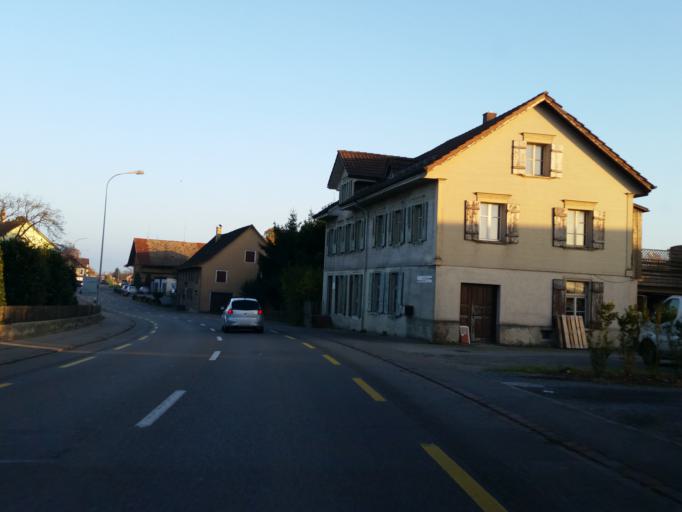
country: CH
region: Thurgau
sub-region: Arbon District
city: Egnach
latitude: 47.5376
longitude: 9.3886
